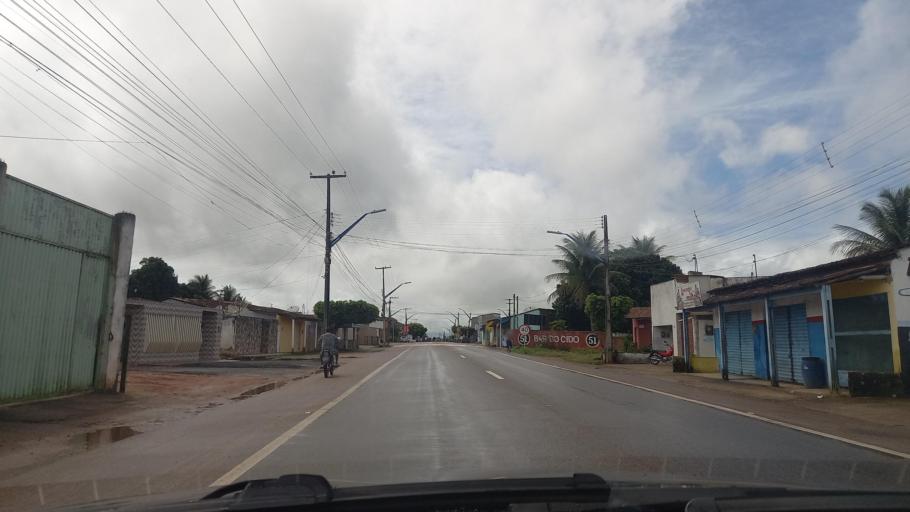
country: BR
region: Alagoas
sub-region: Limoeiro De Anadia
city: Limoeiro de Anadia
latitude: -9.7584
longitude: -36.5584
